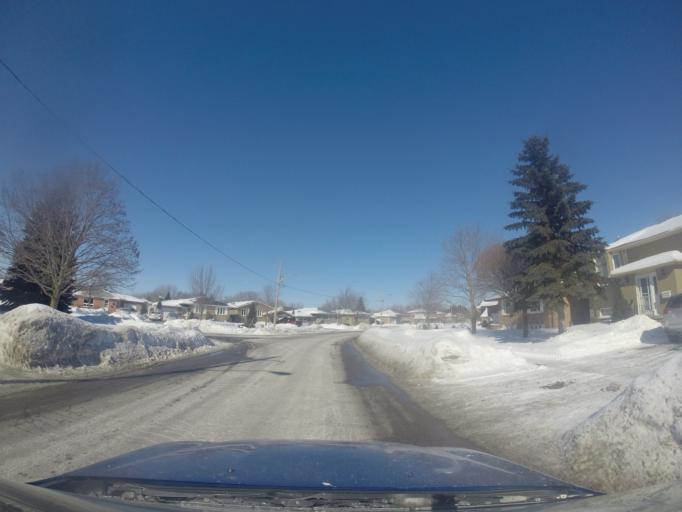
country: CA
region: Ontario
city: Omemee
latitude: 44.3412
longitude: -78.7532
